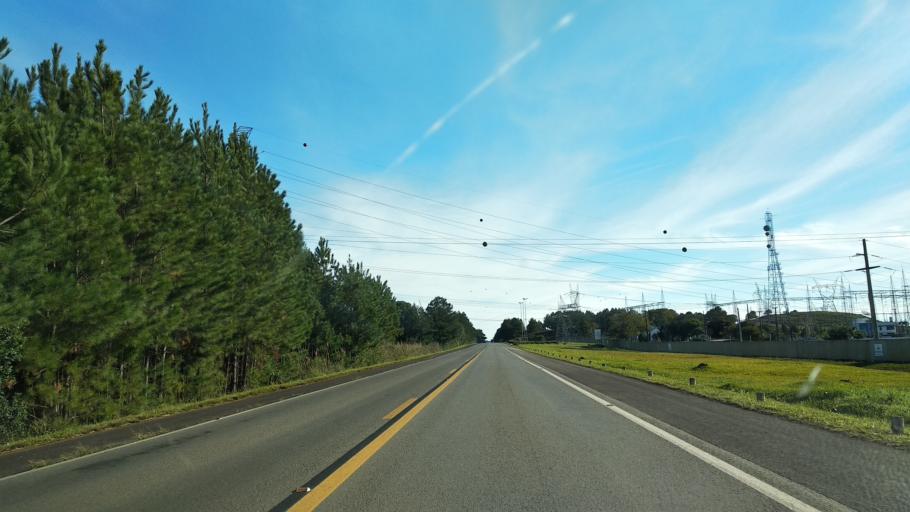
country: BR
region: Santa Catarina
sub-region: Celso Ramos
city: Celso Ramos
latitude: -27.5404
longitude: -51.4134
